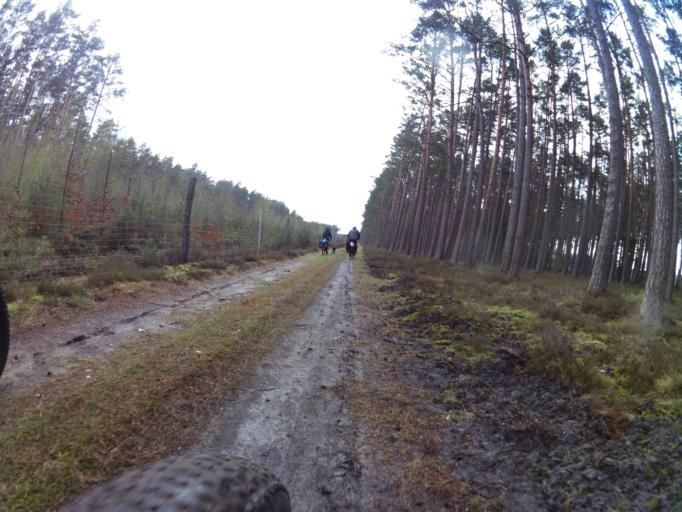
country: PL
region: Pomeranian Voivodeship
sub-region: Powiat slupski
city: Kepice
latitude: 54.3084
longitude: 16.8262
